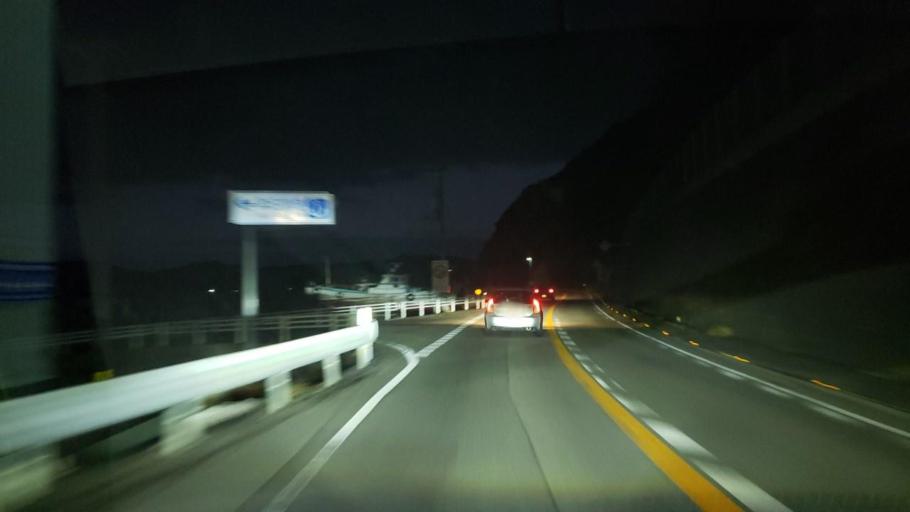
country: JP
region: Tokushima
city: Narutocho-mitsuishi
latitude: 34.2238
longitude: 134.5462
